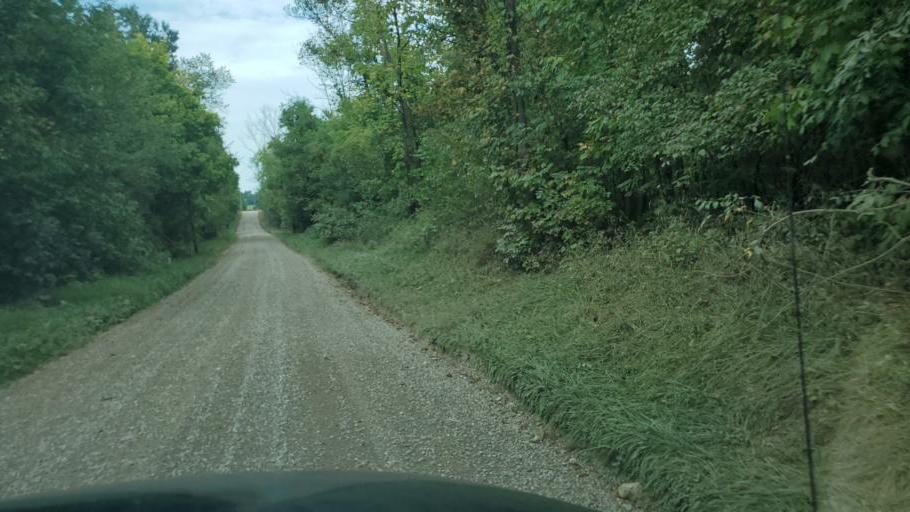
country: US
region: Ohio
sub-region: Muskingum County
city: Frazeysburg
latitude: 39.9696
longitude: -82.2123
